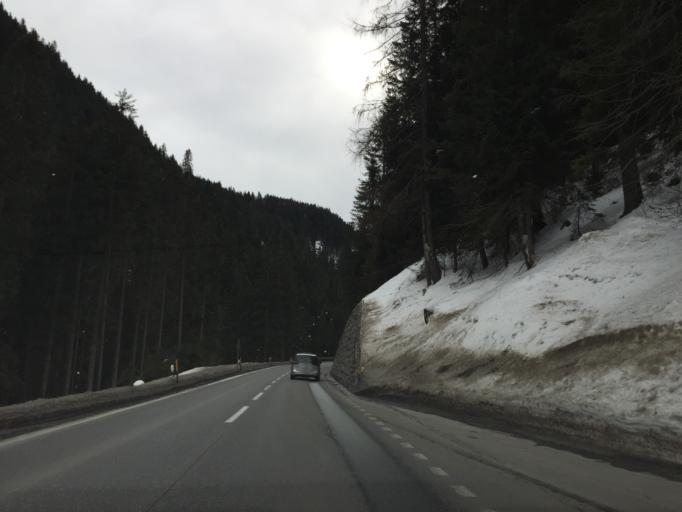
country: CH
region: Grisons
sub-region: Praettigau/Davos District
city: Davos
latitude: 46.8456
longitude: 9.8817
